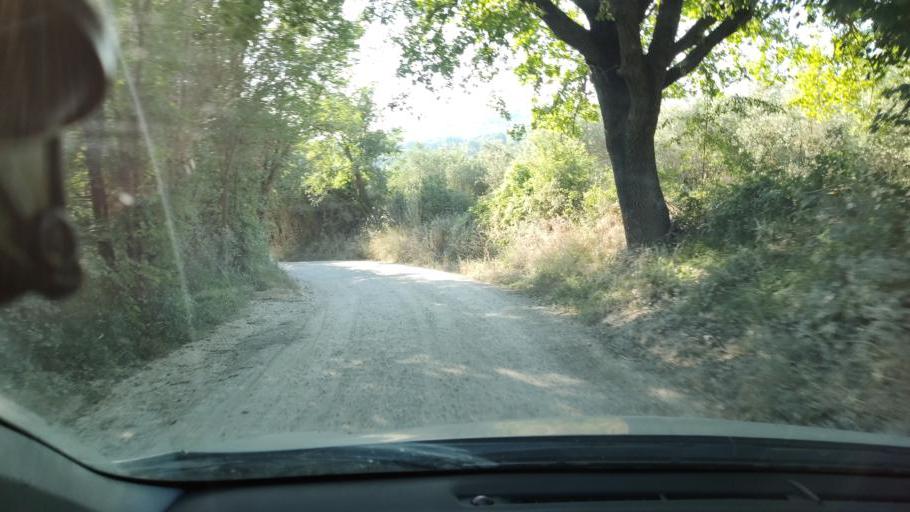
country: IT
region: Umbria
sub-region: Provincia di Terni
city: Amelia
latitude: 42.5453
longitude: 12.3927
